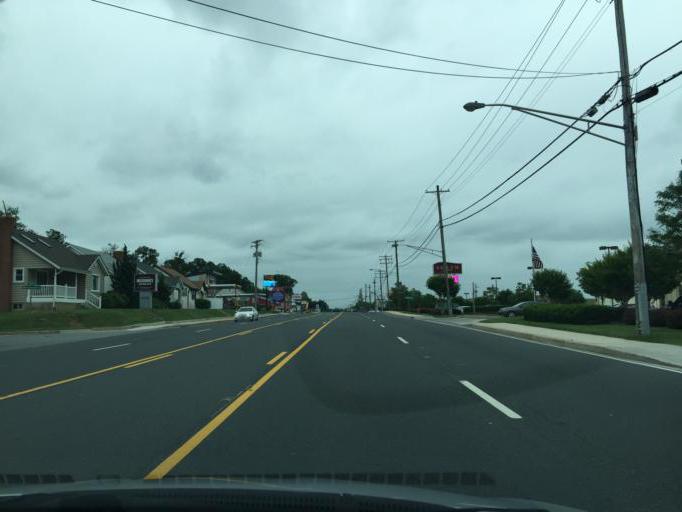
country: US
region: Maryland
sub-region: Baltimore County
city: Timonium
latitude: 39.4382
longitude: -76.6252
